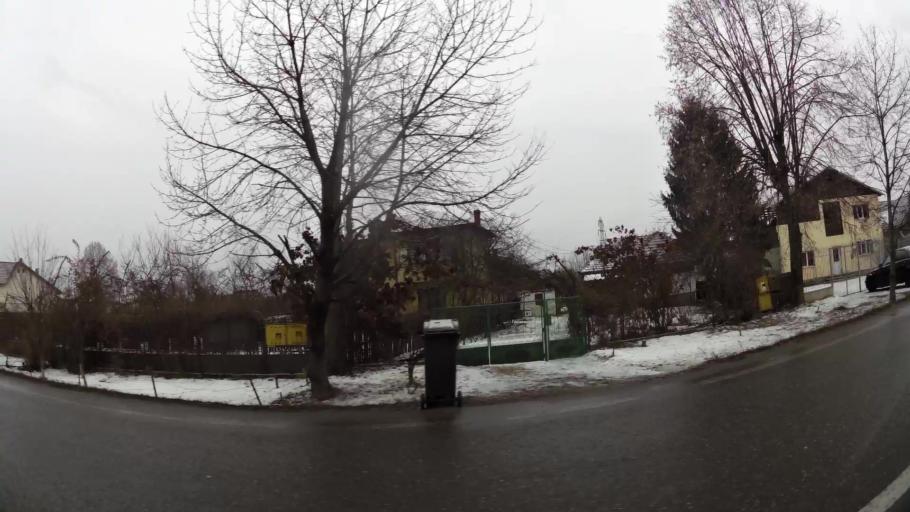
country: RO
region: Dambovita
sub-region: Comuna Aninoasa
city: Viforata
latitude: 44.9443
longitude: 25.4865
